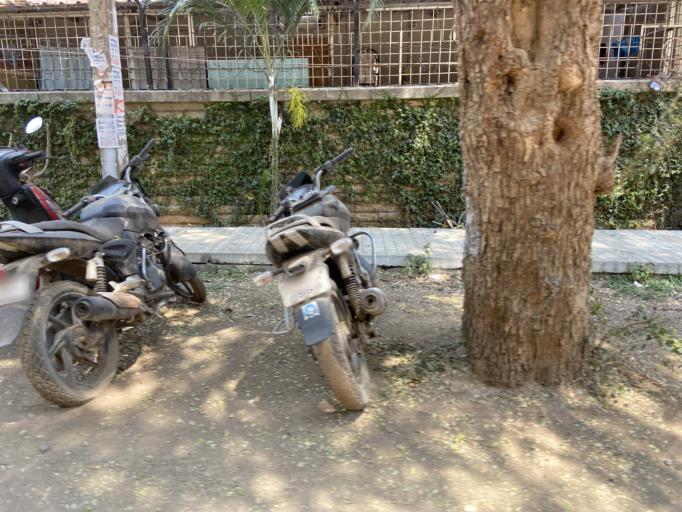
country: IN
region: Karnataka
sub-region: Bangalore Urban
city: Bangalore
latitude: 12.9692
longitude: 77.6835
